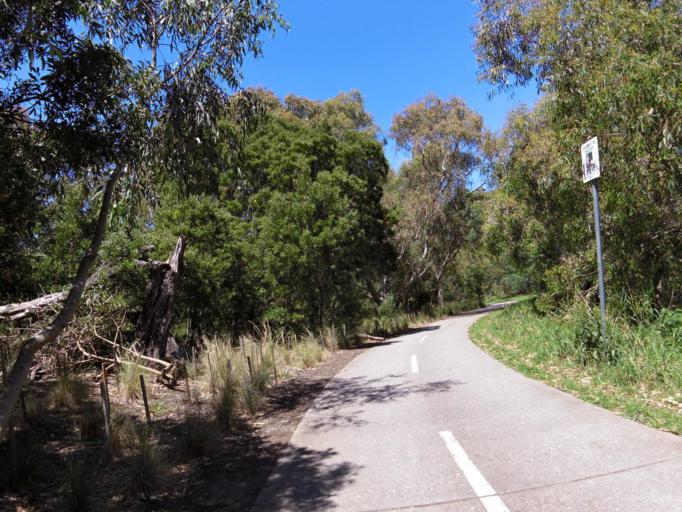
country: AU
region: Victoria
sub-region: Moreland
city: Coburg
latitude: -37.7506
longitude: 144.9813
